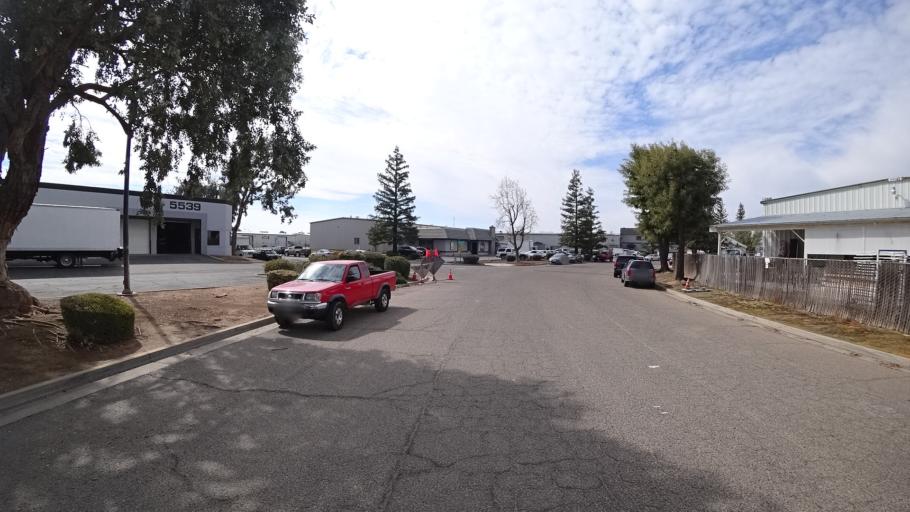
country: US
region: California
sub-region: Fresno County
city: West Park
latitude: 36.8149
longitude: -119.8902
